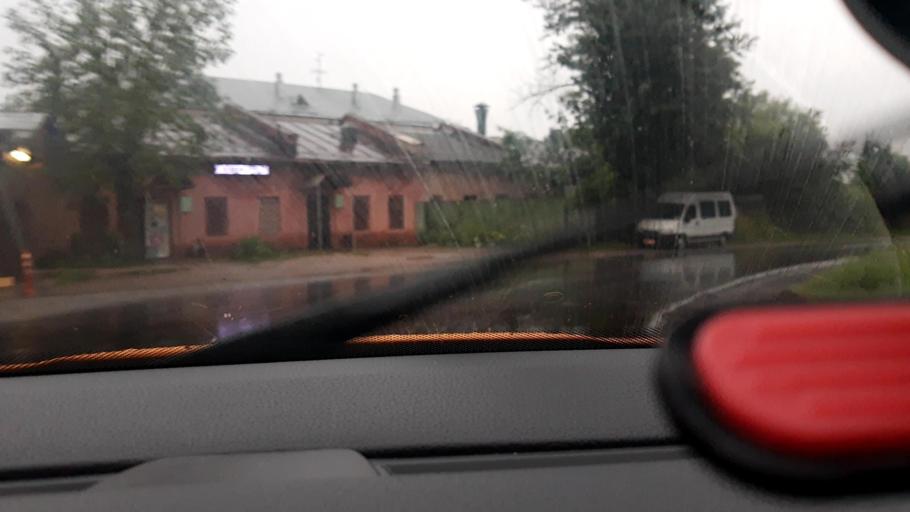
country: RU
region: Moskovskaya
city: Andreyevka
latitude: 55.9984
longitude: 37.1281
